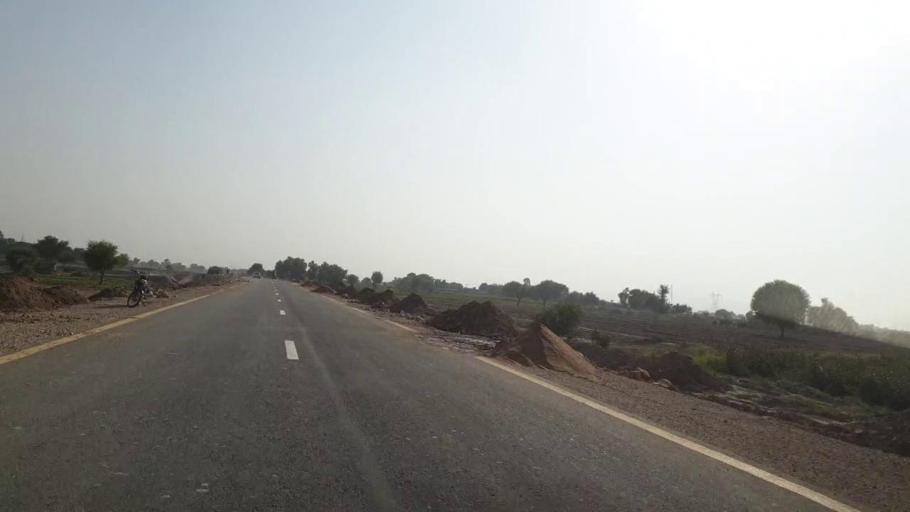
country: PK
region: Sindh
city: Bhan
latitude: 26.4961
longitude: 67.7804
